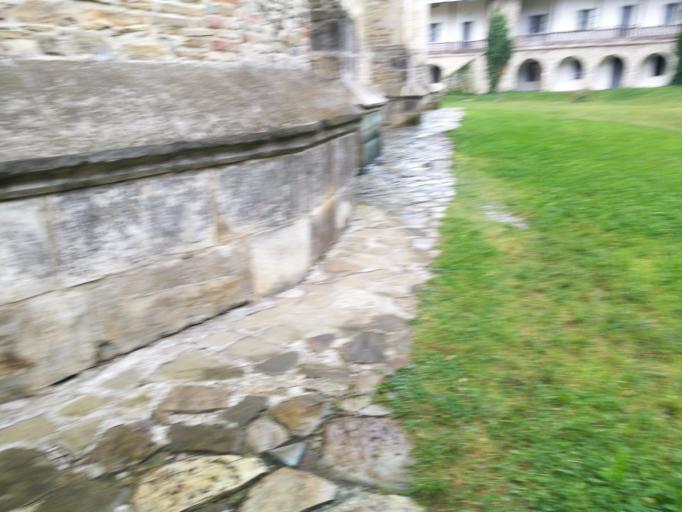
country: RO
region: Neamt
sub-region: Comuna Vanatori Neamt
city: Nemtisor
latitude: 47.2637
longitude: 26.2095
